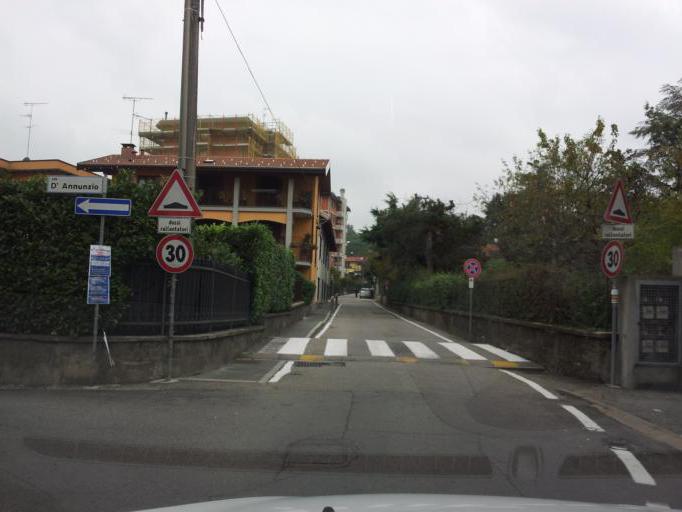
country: IT
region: Lombardy
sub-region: Provincia di Varese
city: Sesto Calende
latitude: 45.7311
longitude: 8.6365
